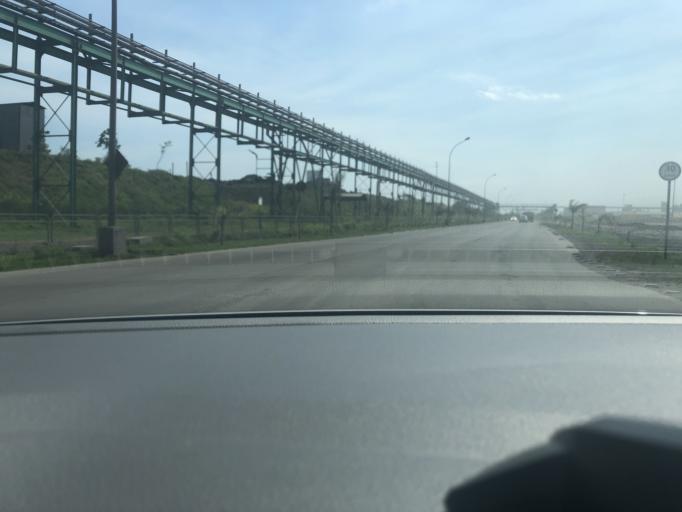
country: BR
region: Rio de Janeiro
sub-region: Itaguai
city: Itaguai
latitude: -22.9110
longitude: -43.7295
